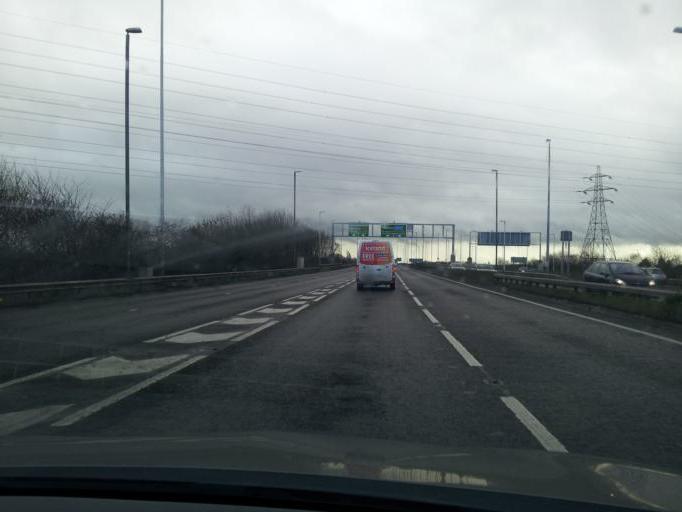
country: GB
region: England
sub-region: Nottingham
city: Nottingham
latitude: 52.9273
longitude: -1.1675
